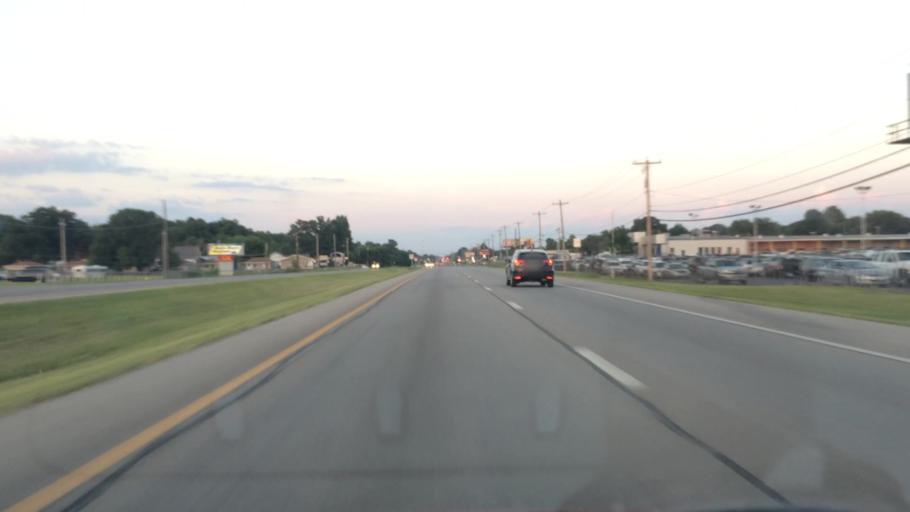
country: US
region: Missouri
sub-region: Greene County
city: Springfield
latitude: 37.1829
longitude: -93.3402
